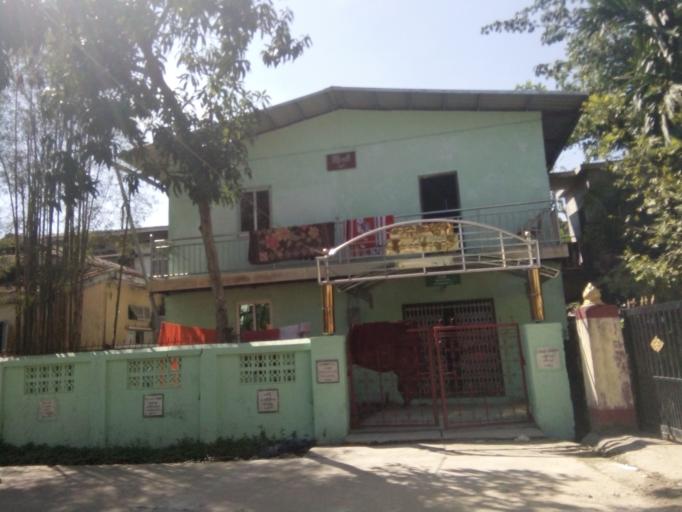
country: MM
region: Yangon
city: Yangon
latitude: 16.9197
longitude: 96.1588
